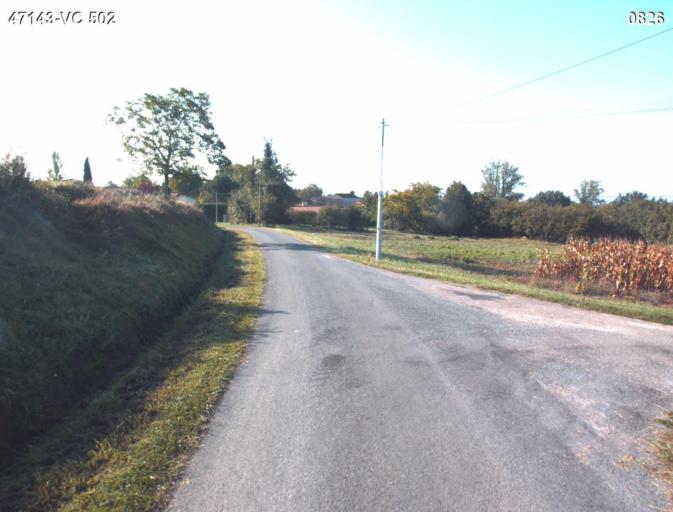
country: FR
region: Aquitaine
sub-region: Departement du Lot-et-Garonne
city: Vianne
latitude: 44.1709
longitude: 0.3267
